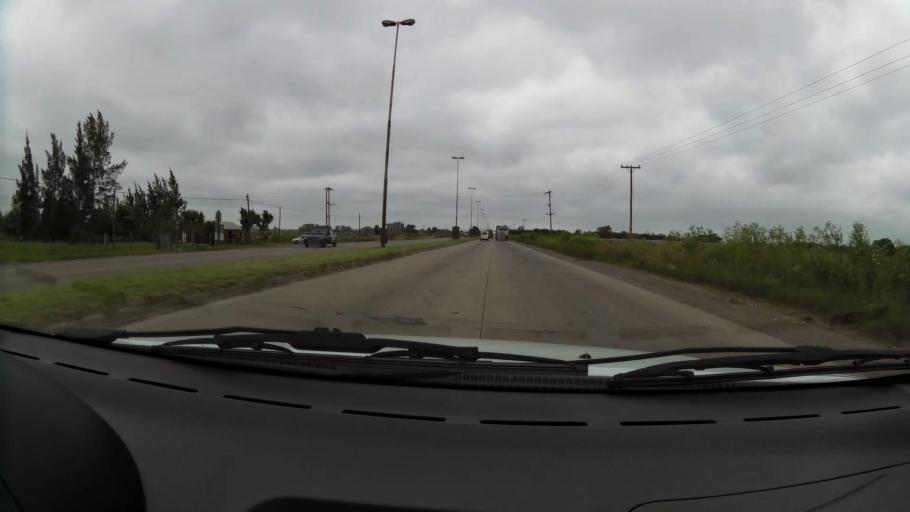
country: AR
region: Buenos Aires
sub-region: Partido de Brandsen
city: Brandsen
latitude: -35.0486
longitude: -58.1066
